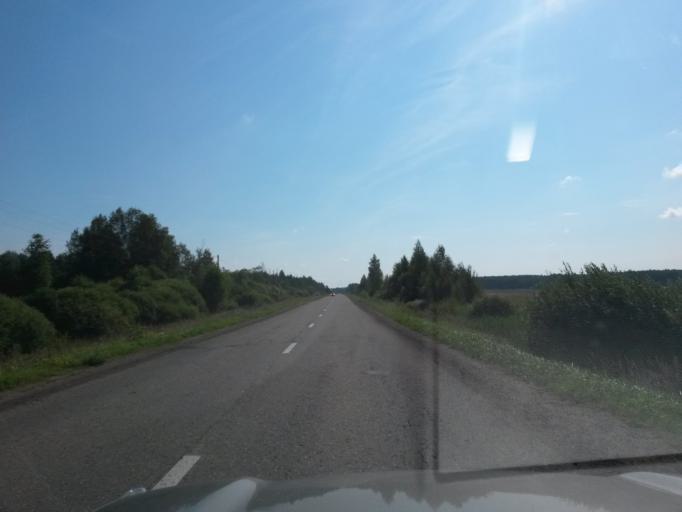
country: RU
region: Jaroslavl
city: Gavrilov-Yam
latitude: 57.3086
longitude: 39.9623
